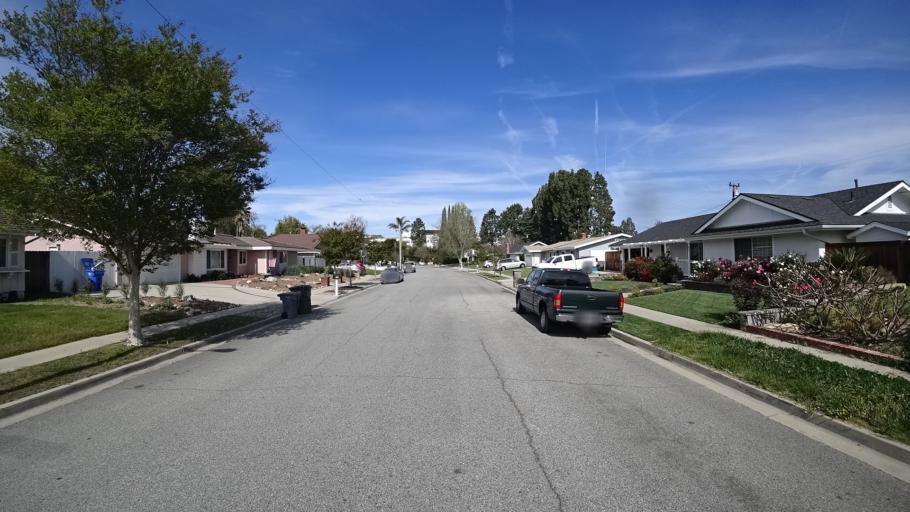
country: US
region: California
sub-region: Ventura County
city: Thousand Oaks
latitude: 34.2068
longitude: -118.8792
